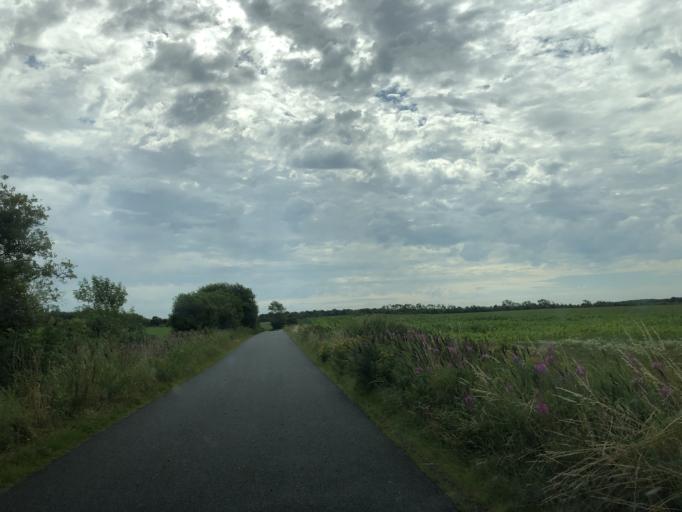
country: DK
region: Central Jutland
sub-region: Holstebro Kommune
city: Ulfborg
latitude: 56.3058
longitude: 8.4452
